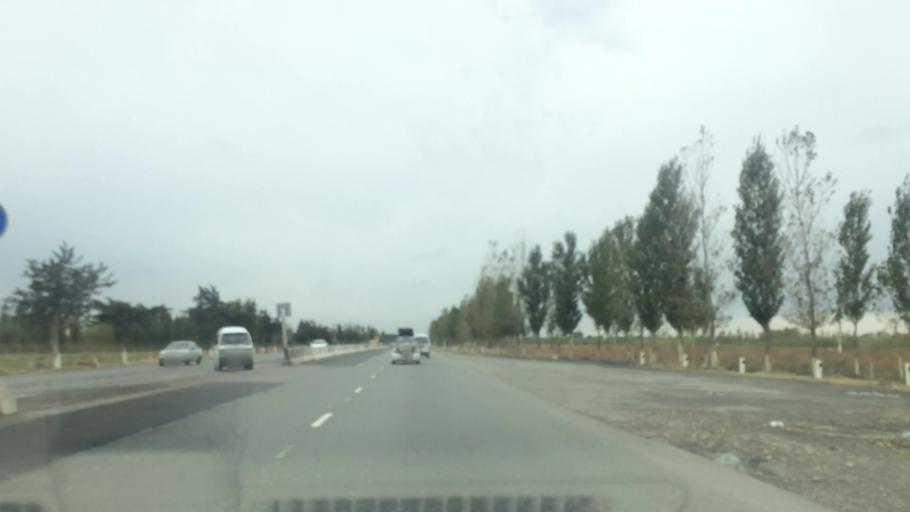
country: UZ
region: Samarqand
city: Bulung'ur
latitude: 39.7889
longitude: 67.3159
